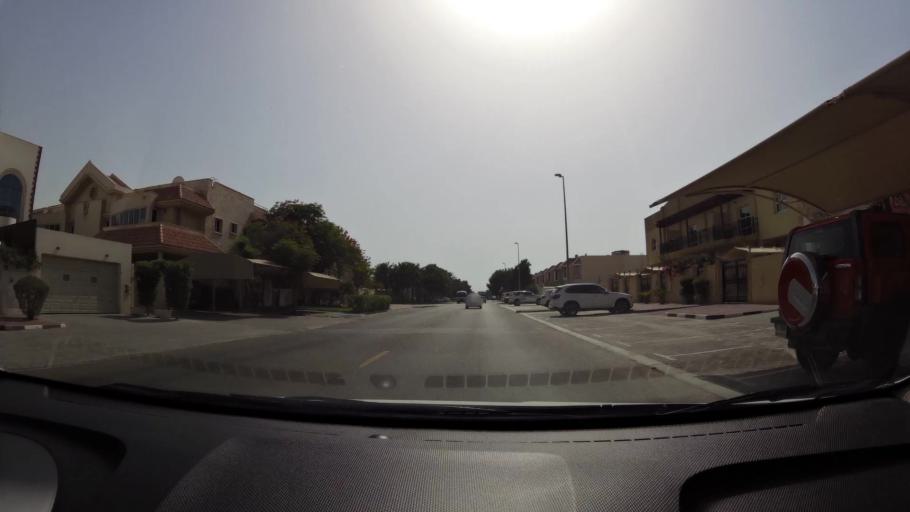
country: AE
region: Ash Shariqah
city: Sharjah
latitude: 25.2408
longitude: 55.3566
